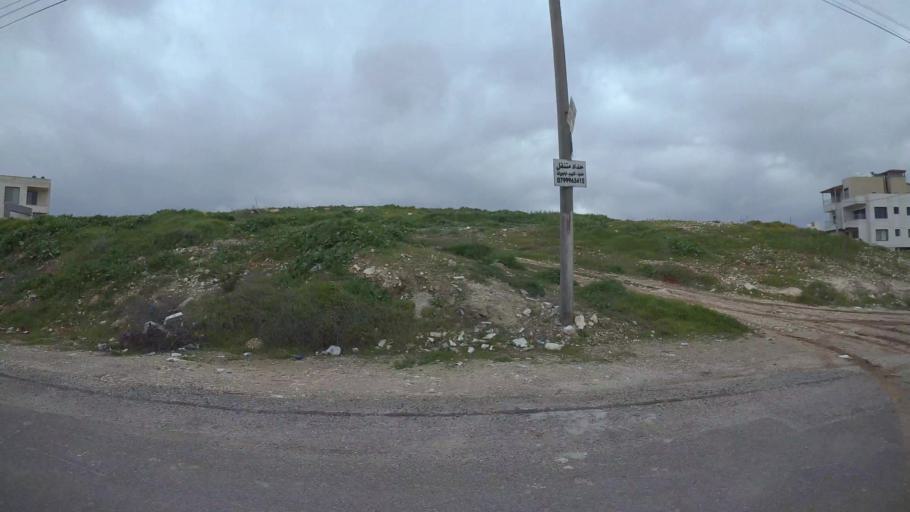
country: JO
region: Amman
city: Al Jubayhah
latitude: 31.9939
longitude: 35.8353
